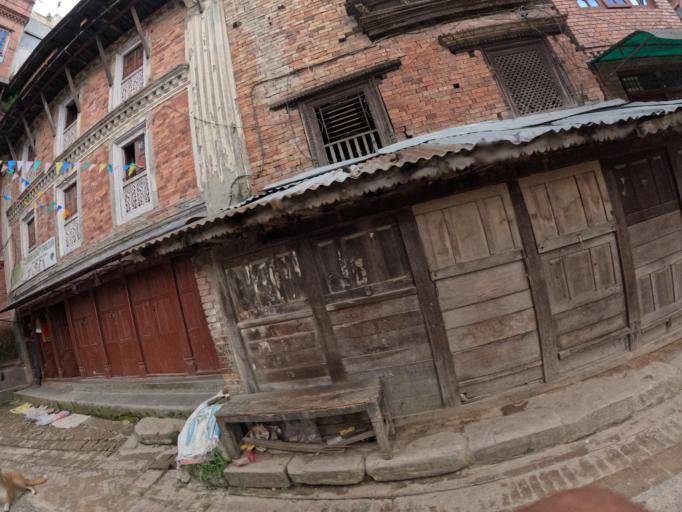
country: NP
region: Central Region
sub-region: Bagmati Zone
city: Bhaktapur
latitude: 27.6802
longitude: 85.3860
